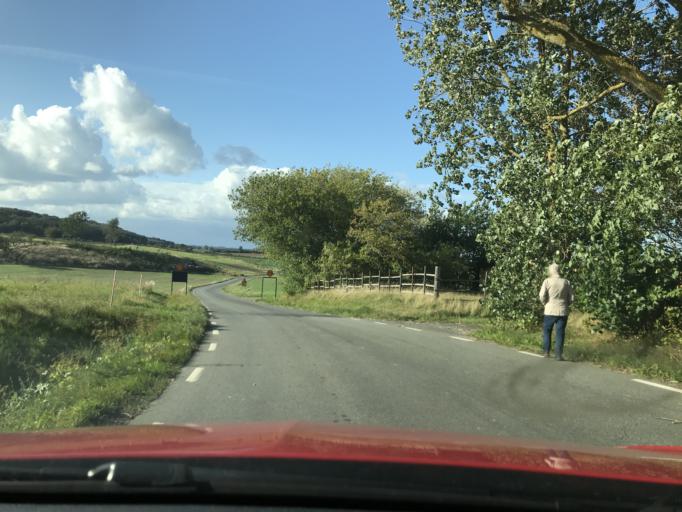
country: SE
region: Skane
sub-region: Kristianstads Kommun
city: Degeberga
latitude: 55.8415
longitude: 14.0871
